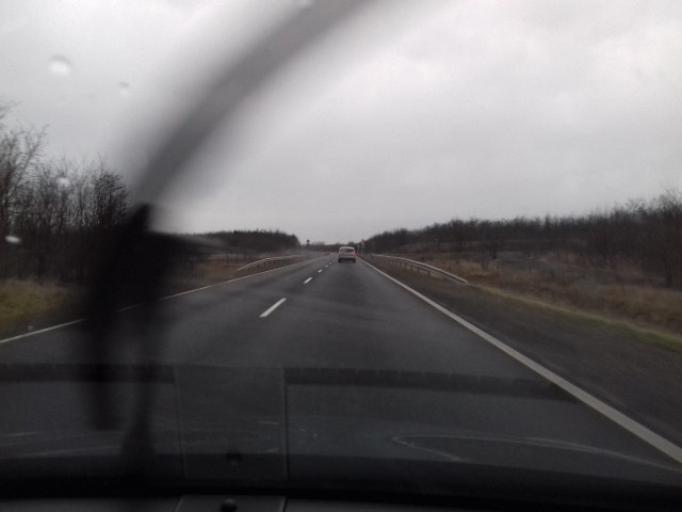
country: HU
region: Szabolcs-Szatmar-Bereg
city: Nyirpazony
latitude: 47.9967
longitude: 21.8298
